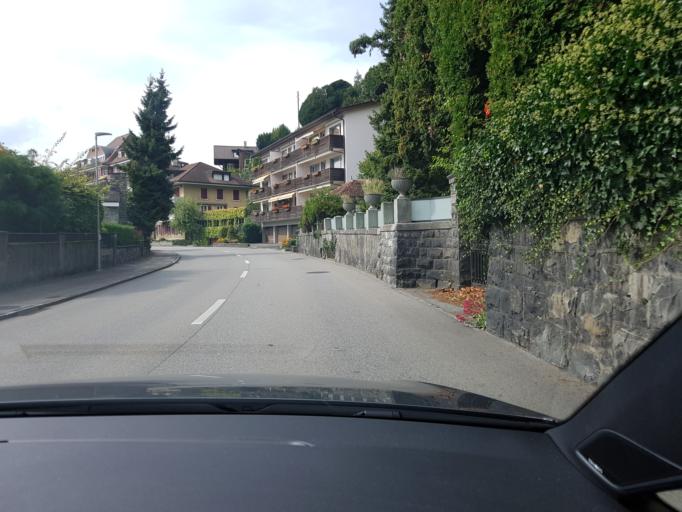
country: CH
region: Bern
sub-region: Thun District
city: Sigriswil
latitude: 46.7143
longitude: 7.6971
